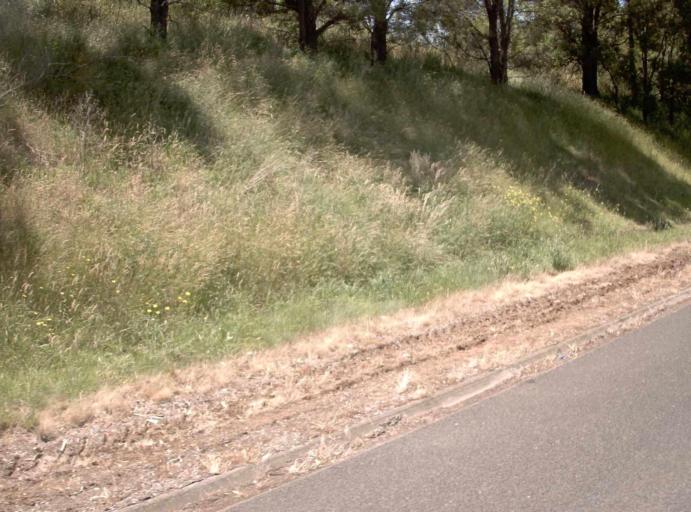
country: AU
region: Victoria
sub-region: Baw Baw
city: Warragul
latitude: -38.1565
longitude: 145.9034
